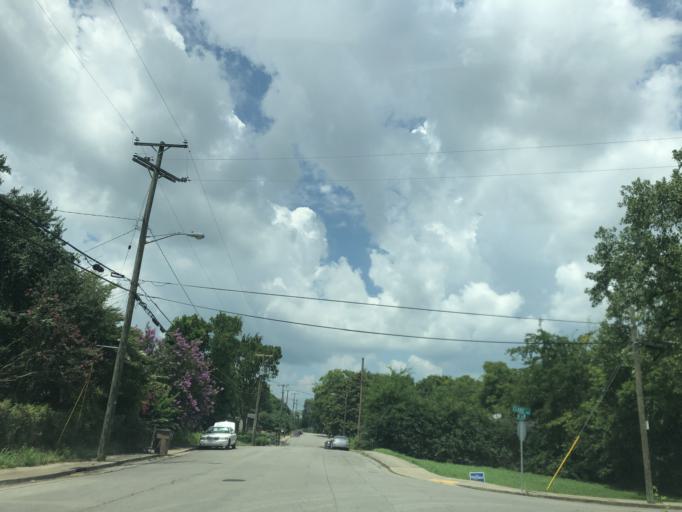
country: US
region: Tennessee
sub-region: Davidson County
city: Nashville
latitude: 36.1615
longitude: -86.8230
